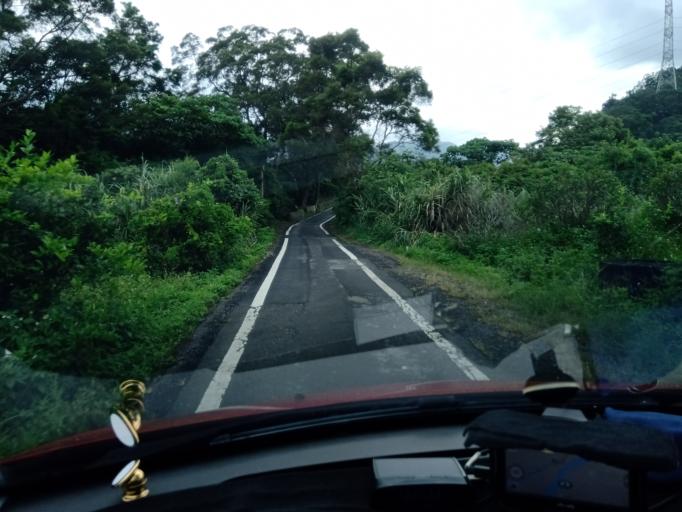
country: TW
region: Taiwan
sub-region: Yilan
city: Yilan
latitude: 24.7809
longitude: 121.7138
